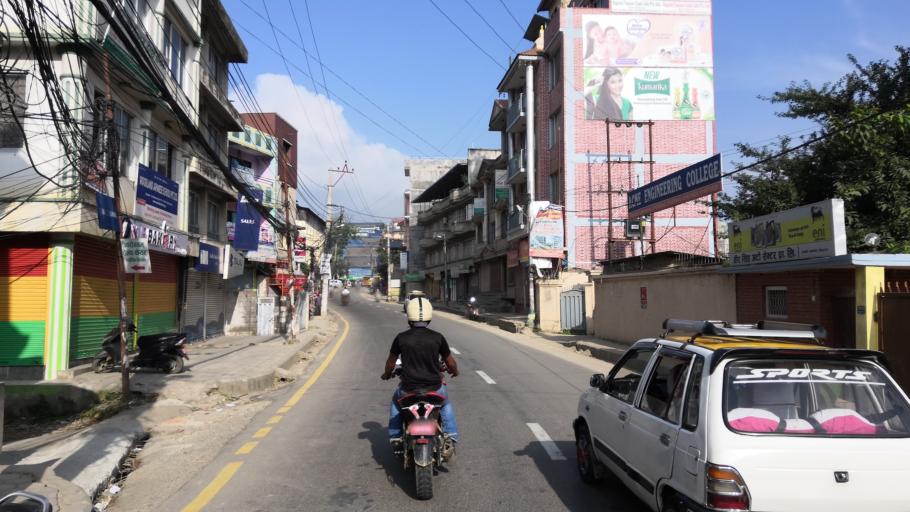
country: NP
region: Central Region
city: Kirtipur
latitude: 27.7078
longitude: 85.2845
